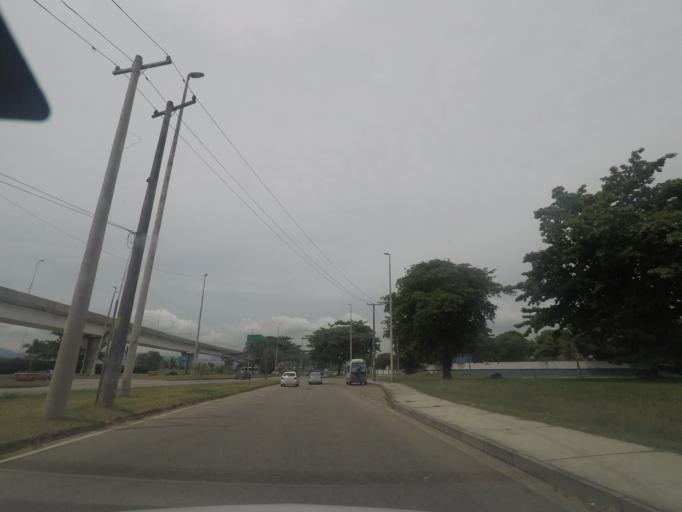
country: BR
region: Rio de Janeiro
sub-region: Rio De Janeiro
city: Rio de Janeiro
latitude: -22.8239
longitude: -43.2318
